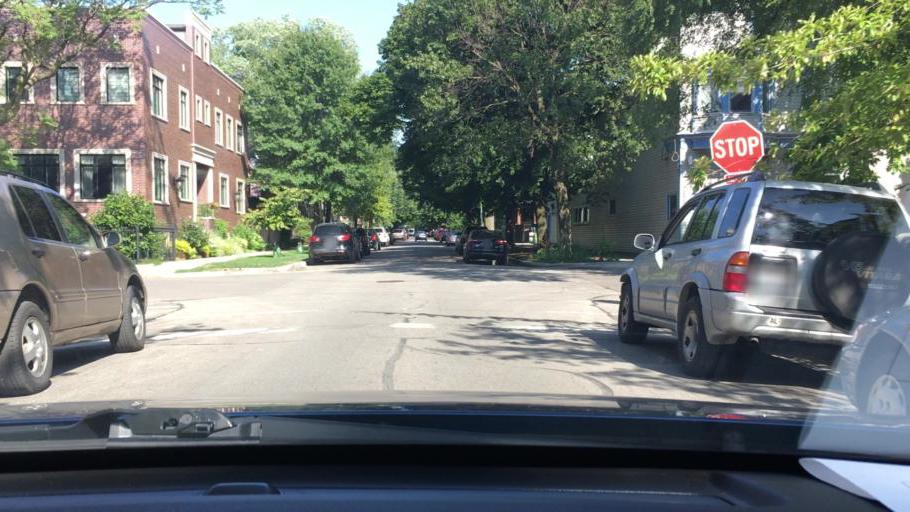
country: US
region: Illinois
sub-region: Cook County
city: Lincolnwood
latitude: 41.9413
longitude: -87.6835
